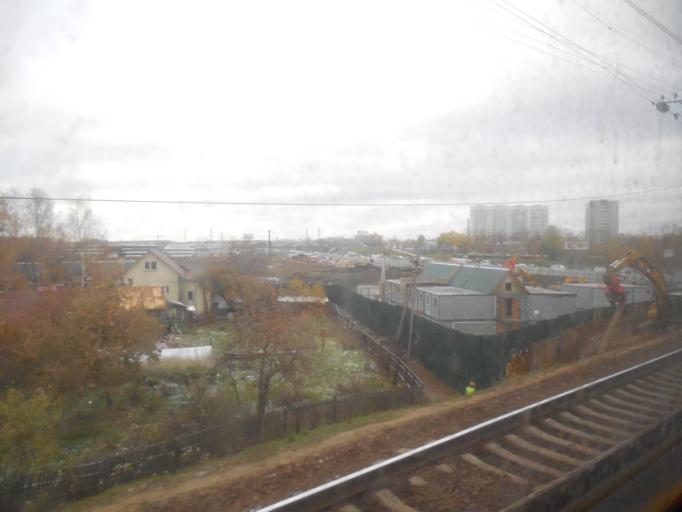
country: RU
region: Moskovskaya
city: Marfino
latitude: 55.7190
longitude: 37.3841
